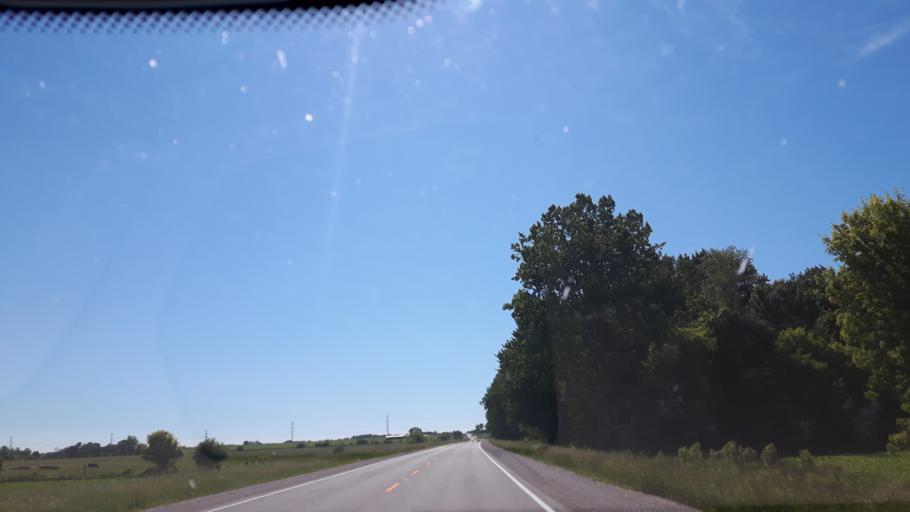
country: CA
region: Ontario
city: Bluewater
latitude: 43.4252
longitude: -81.5860
